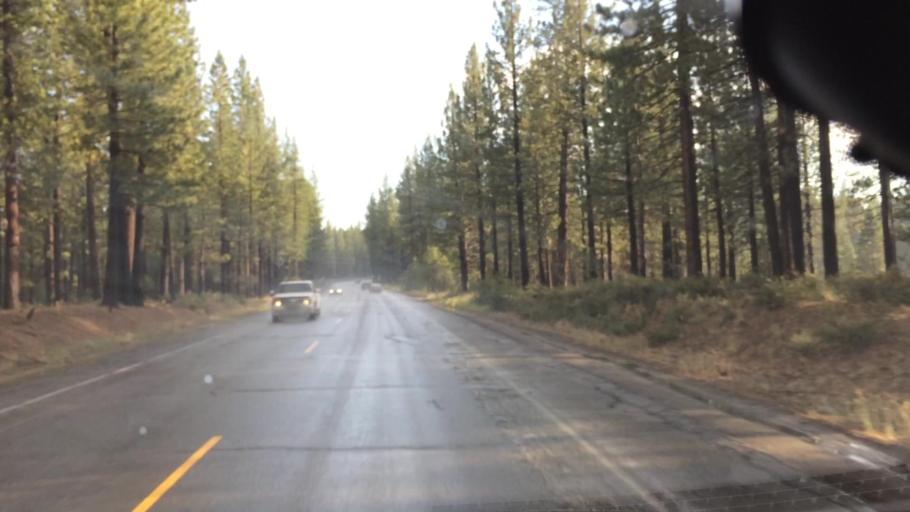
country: US
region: California
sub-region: El Dorado County
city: South Lake Tahoe
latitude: 38.8940
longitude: -119.9728
